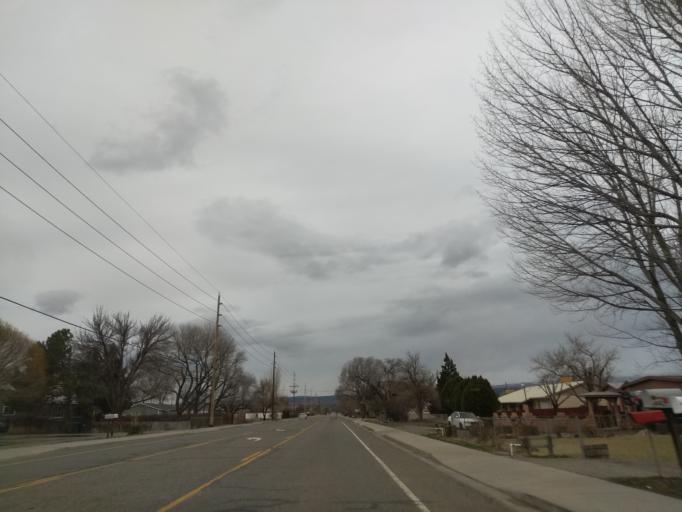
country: US
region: Colorado
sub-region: Mesa County
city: Fruitvale
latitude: 39.0693
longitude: -108.4966
